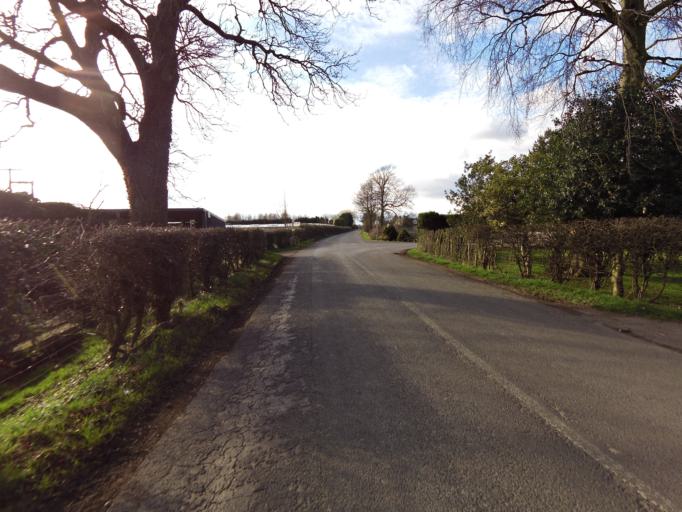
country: GB
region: England
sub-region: East Riding of Yorkshire
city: Snaith
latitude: 53.7080
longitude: -1.0548
